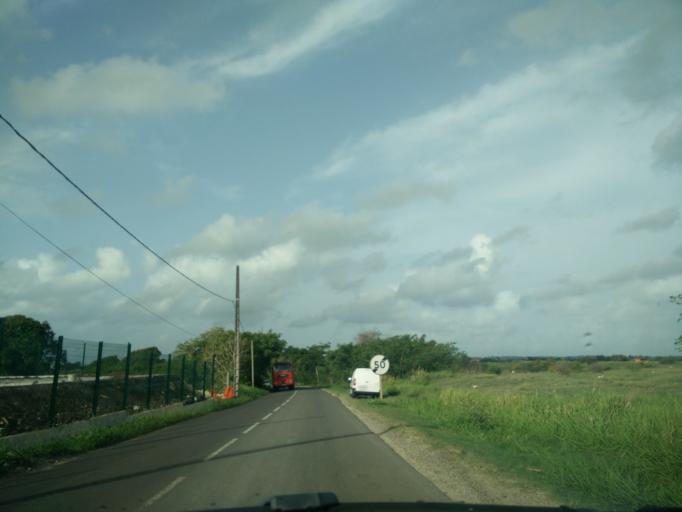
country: GP
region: Guadeloupe
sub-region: Guadeloupe
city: Le Moule
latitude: 16.3127
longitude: -61.3654
